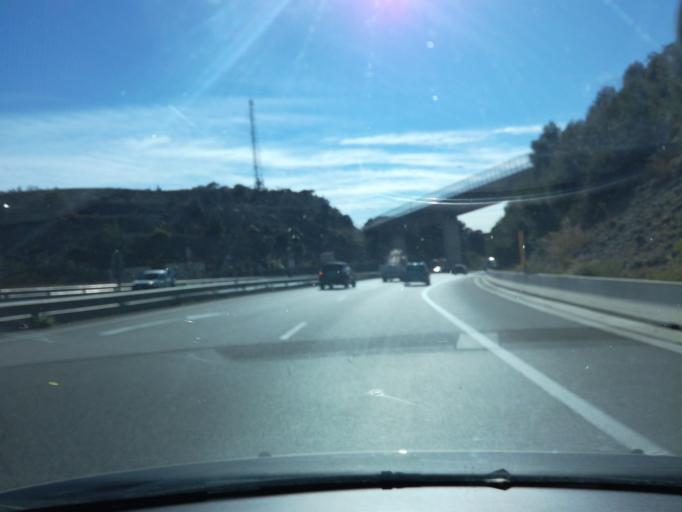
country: FR
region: Provence-Alpes-Cote d'Azur
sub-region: Departement des Alpes-Maritimes
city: Colomars
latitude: 43.7240
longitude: 7.2288
